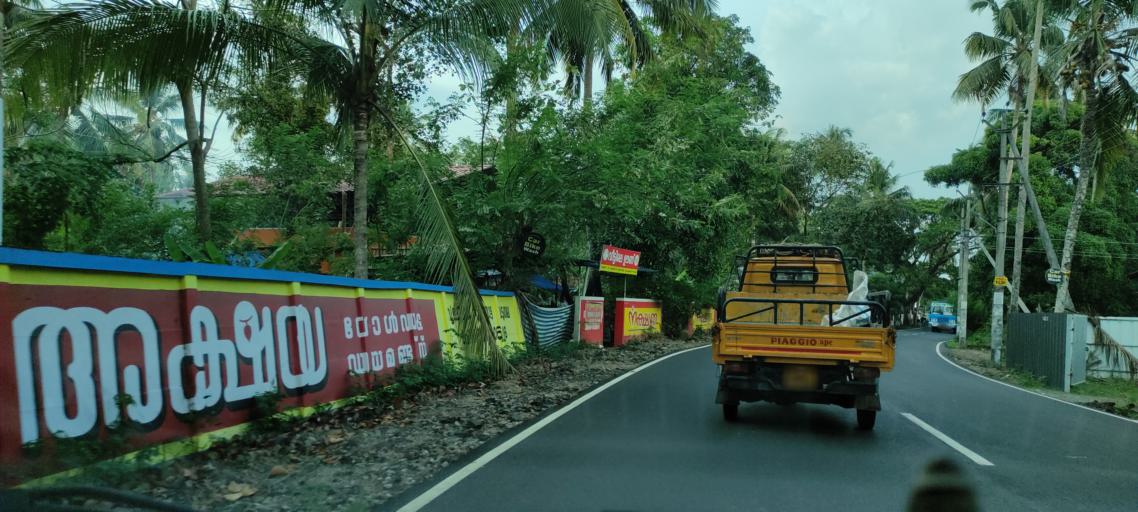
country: IN
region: Kerala
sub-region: Alappuzha
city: Kutiatodu
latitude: 9.8278
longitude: 76.3422
